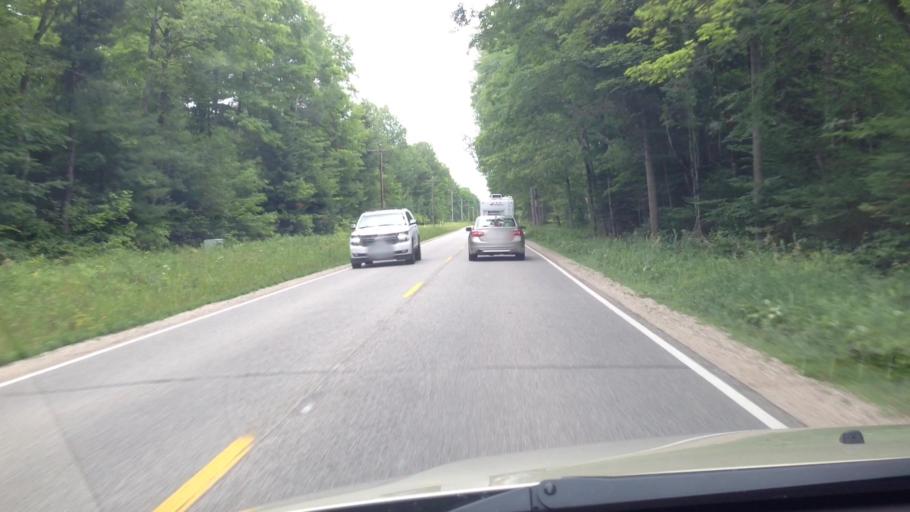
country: US
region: Michigan
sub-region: Mackinac County
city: Saint Ignace
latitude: 46.0568
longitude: -85.1442
